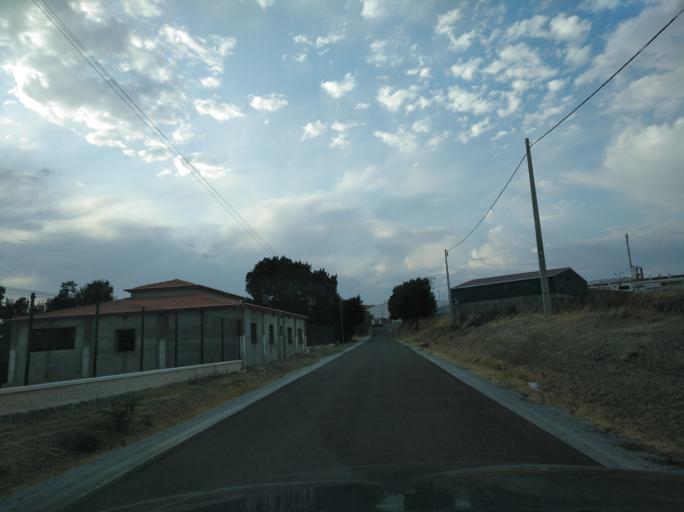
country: PT
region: Portalegre
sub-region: Campo Maior
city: Campo Maior
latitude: 39.0094
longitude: -7.0629
